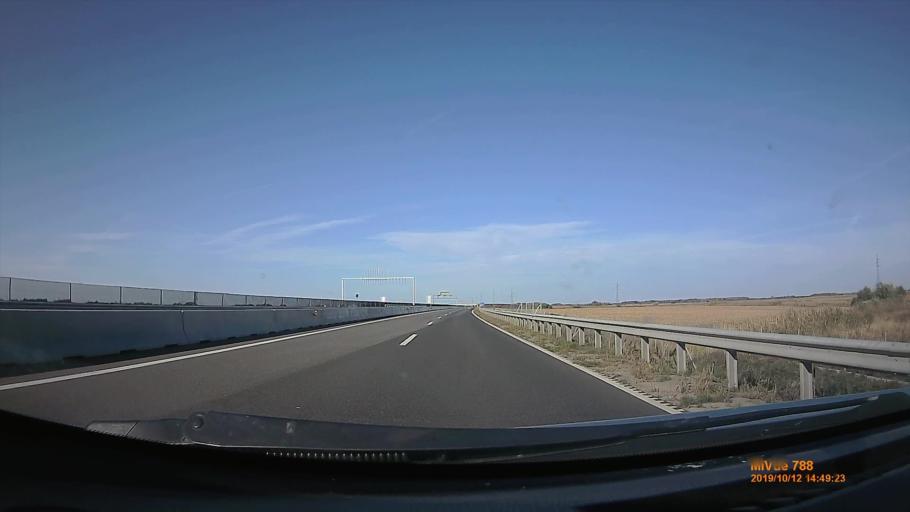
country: HU
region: Hajdu-Bihar
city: Derecske
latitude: 47.3009
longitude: 21.5043
